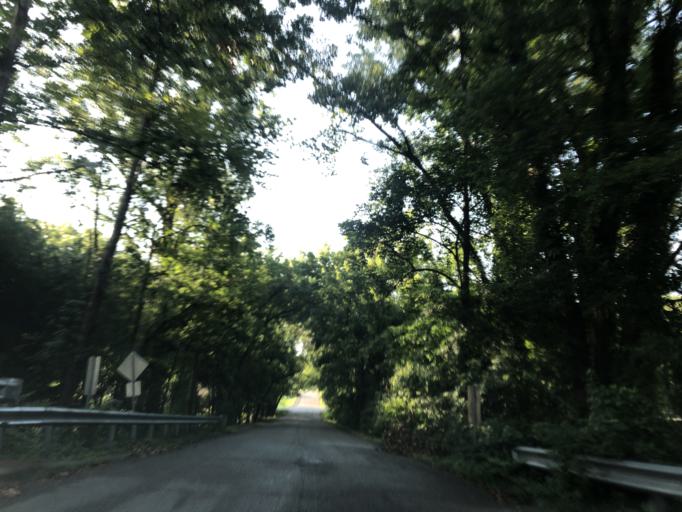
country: US
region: Tennessee
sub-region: Davidson County
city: Lakewood
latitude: 36.1521
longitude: -86.6502
